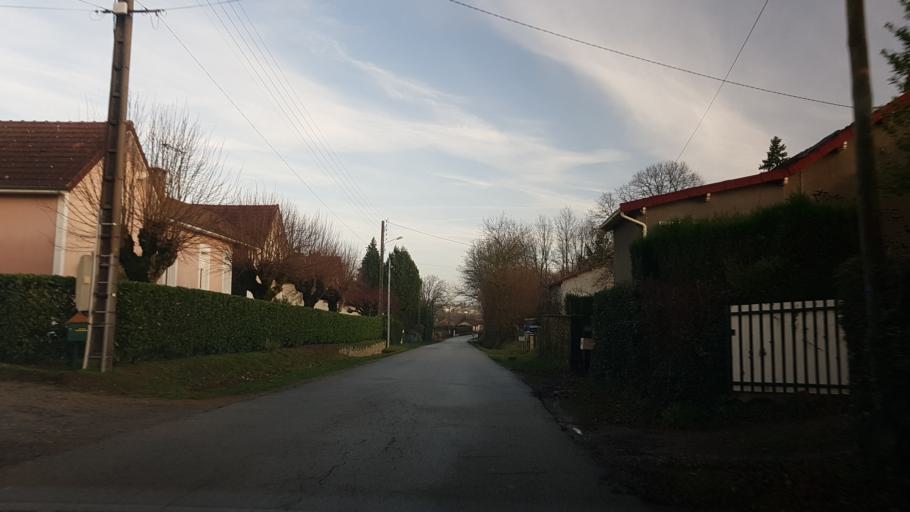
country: FR
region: Limousin
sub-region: Departement de la Haute-Vienne
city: Saint-Junien
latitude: 45.8958
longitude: 0.8711
